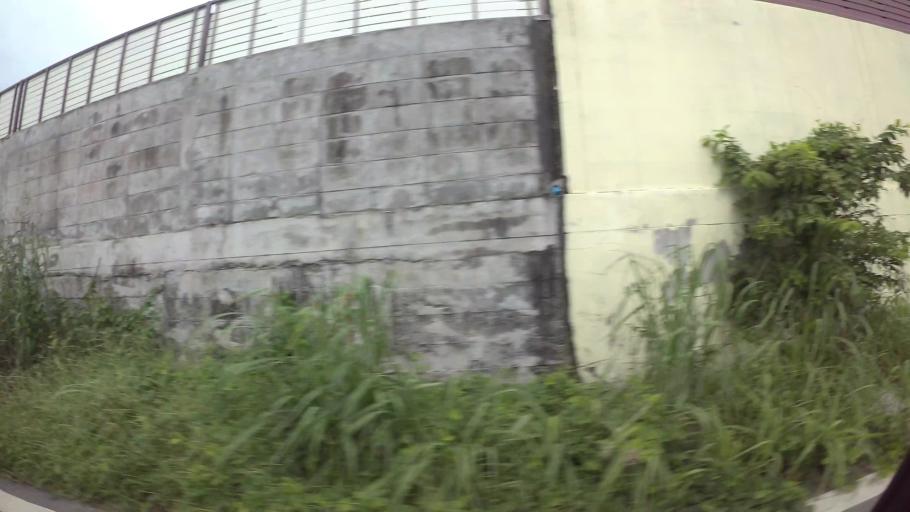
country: TH
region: Chon Buri
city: Si Racha
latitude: 13.1542
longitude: 100.9768
